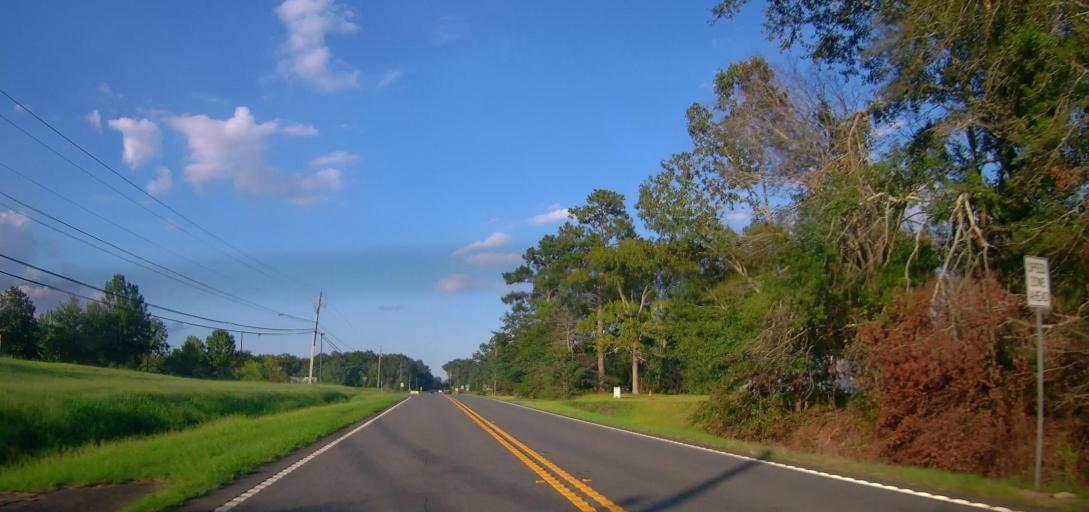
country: US
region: Georgia
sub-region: Crawford County
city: Roberta
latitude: 32.7131
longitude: -84.0214
